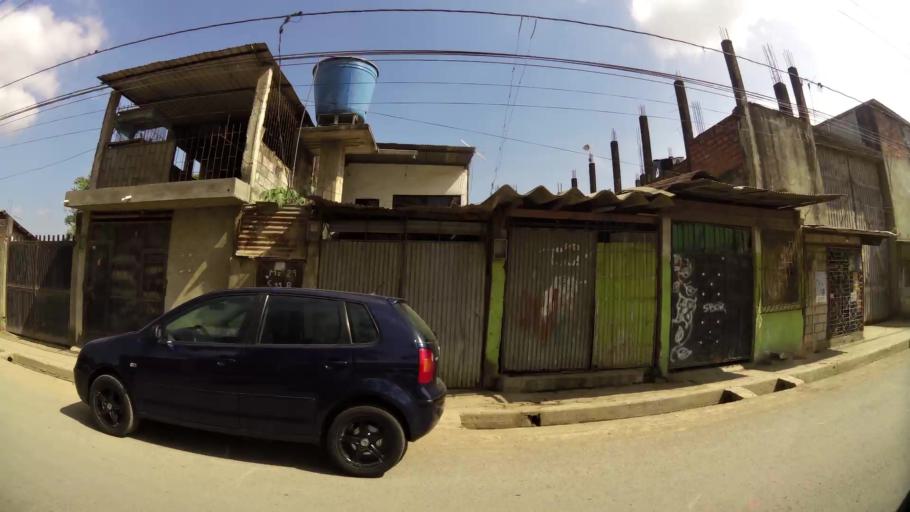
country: EC
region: Guayas
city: Eloy Alfaro
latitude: -2.1675
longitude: -79.8252
